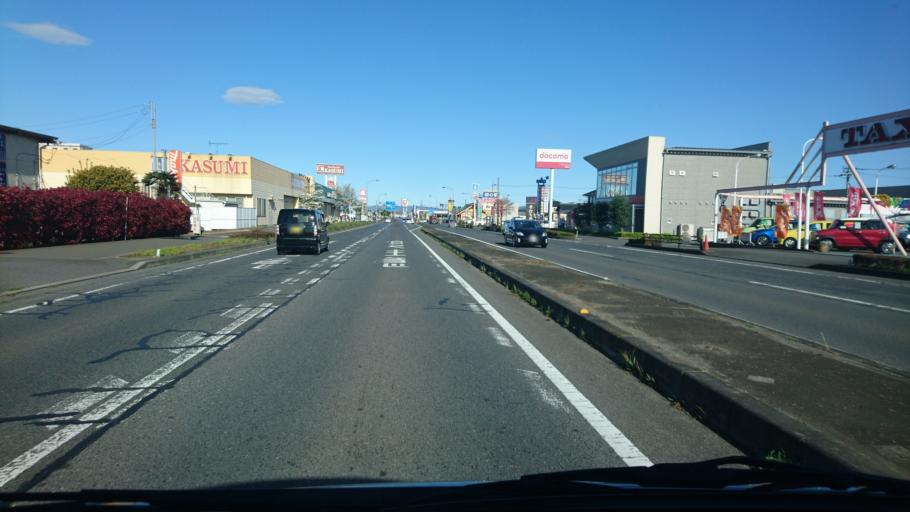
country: JP
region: Ibaraki
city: Yuki
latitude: 36.2865
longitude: 139.8750
